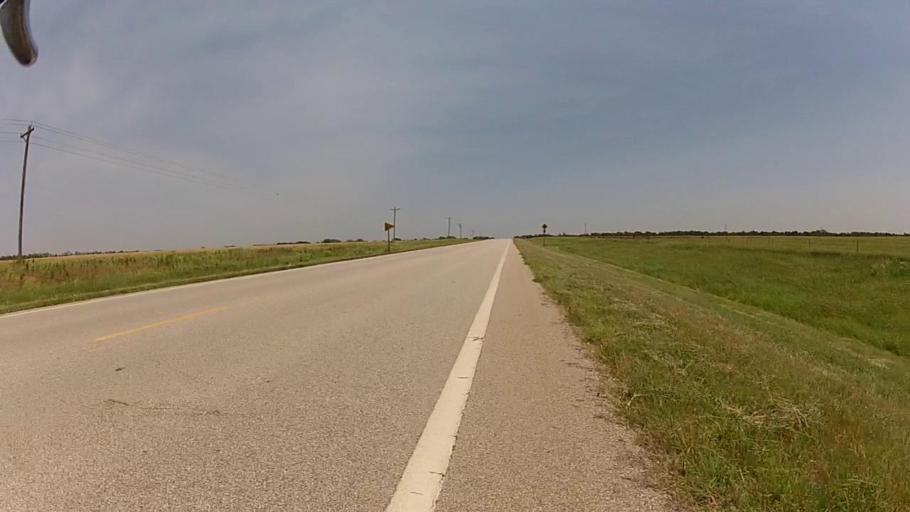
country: US
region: Kansas
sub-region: Cowley County
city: Arkansas City
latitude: 37.0569
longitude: -97.2229
